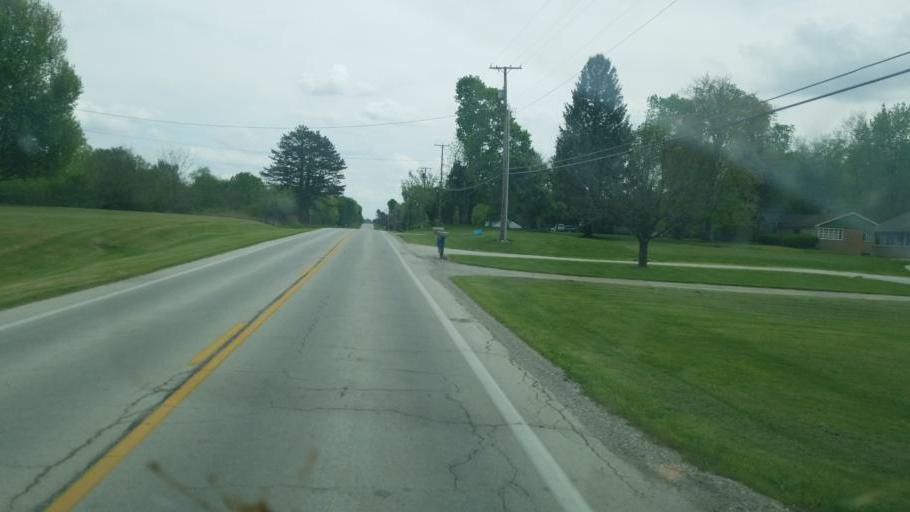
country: US
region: Ohio
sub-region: Seneca County
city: Tiffin
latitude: 41.0951
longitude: -83.1632
